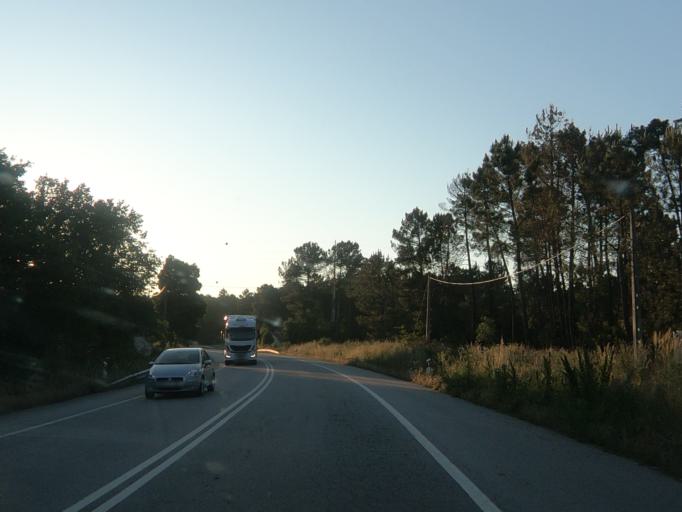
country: PT
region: Viseu
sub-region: Viseu
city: Rio de Loba
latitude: 40.6729
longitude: -7.8608
